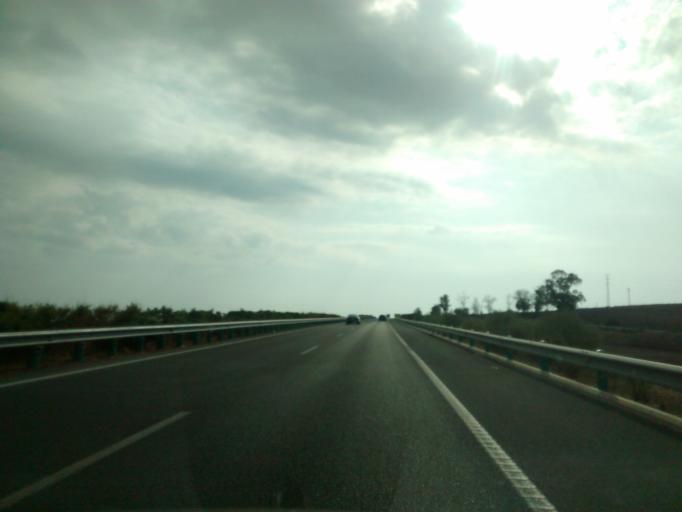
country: ES
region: Andalusia
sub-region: Provincia de Cadiz
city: Arcos de la Frontera
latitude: 36.7346
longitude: -5.8963
